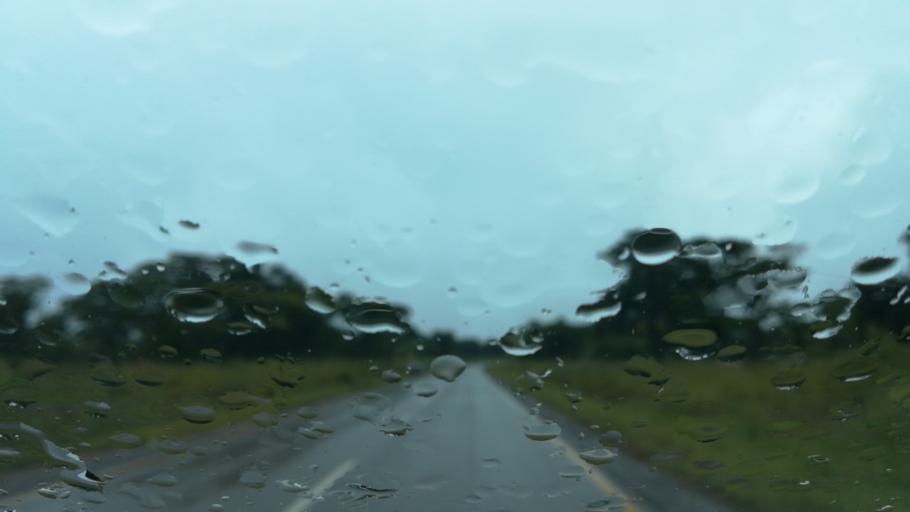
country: ZM
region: Luapula
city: Mwense
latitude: -10.8839
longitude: 28.2149
